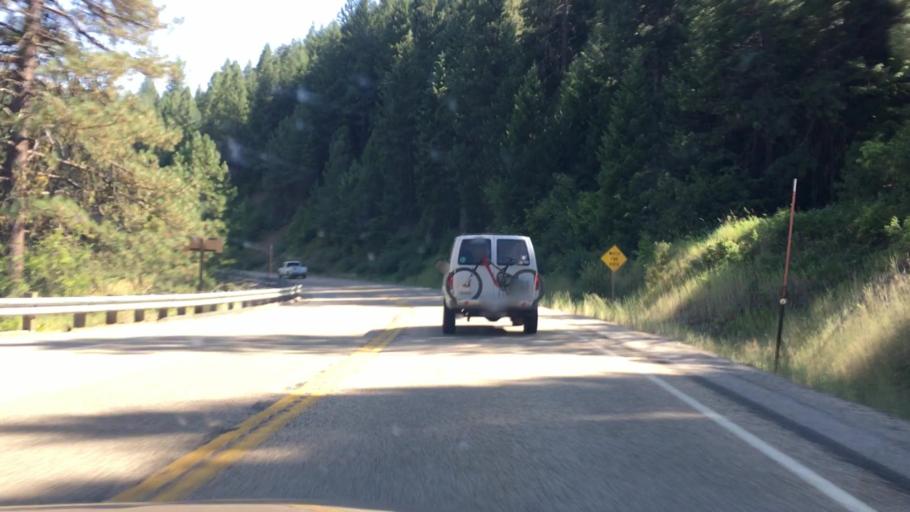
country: US
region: Idaho
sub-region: Valley County
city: Cascade
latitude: 44.1324
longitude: -116.1152
